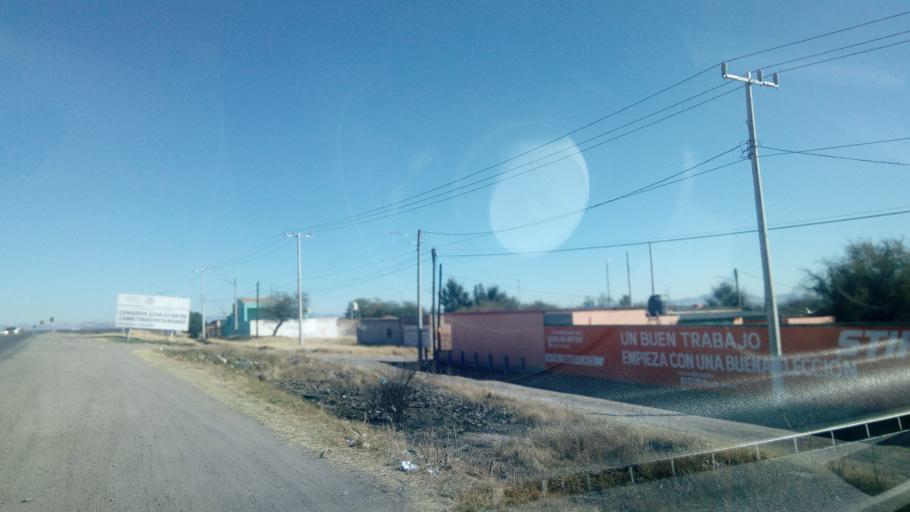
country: MX
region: Durango
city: Victoria de Durango
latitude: 24.1064
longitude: -104.5727
